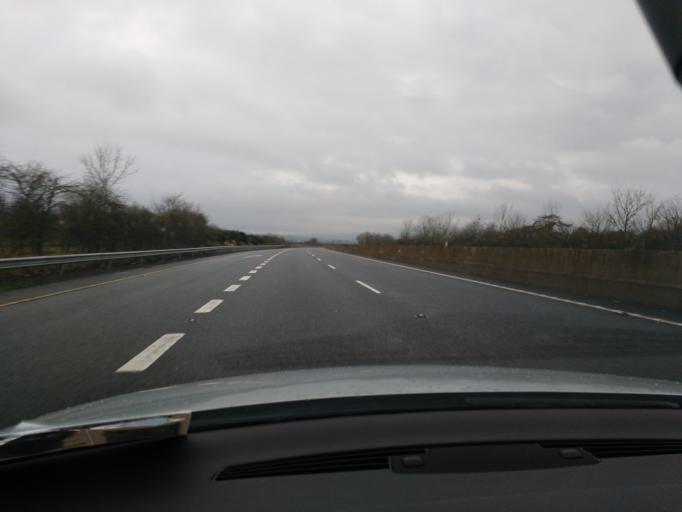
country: IE
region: Munster
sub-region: North Tipperary
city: Nenagh
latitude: 52.8498
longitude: -8.1578
